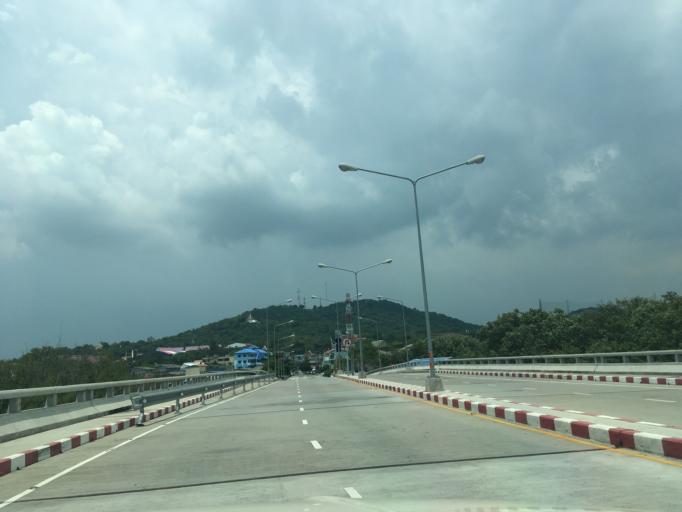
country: TH
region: Chon Buri
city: Chon Buri
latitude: 13.3923
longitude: 100.9833
